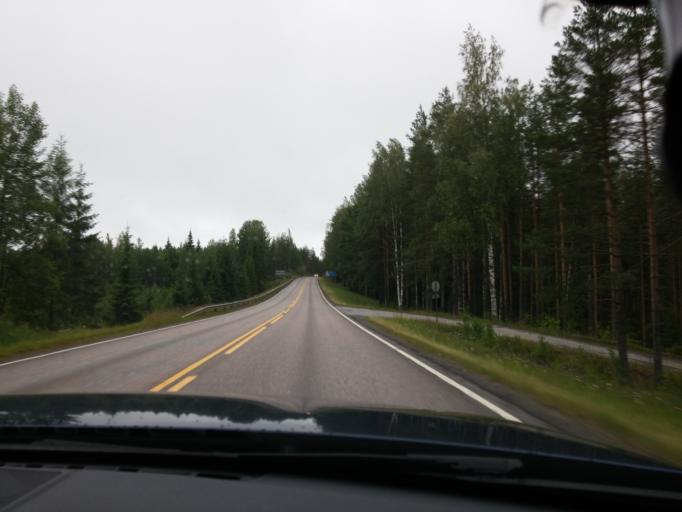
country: FI
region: Pirkanmaa
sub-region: Ylae-Pirkanmaa
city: Vilppula
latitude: 61.9295
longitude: 24.5411
